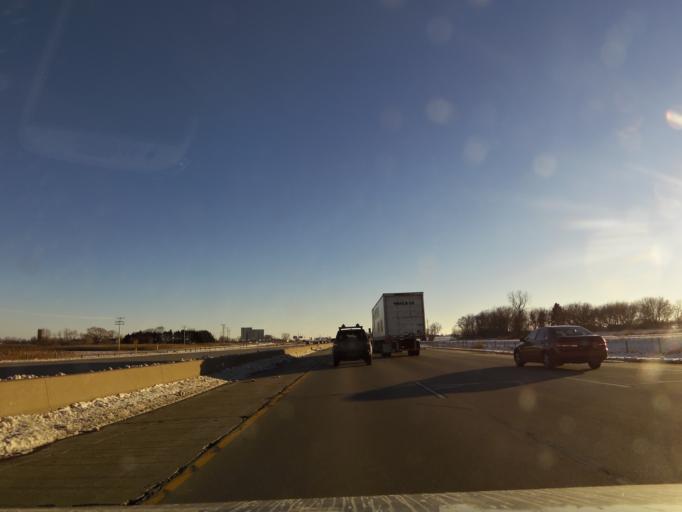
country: US
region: Wisconsin
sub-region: Kenosha County
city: Somers
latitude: 42.6505
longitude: -87.9528
